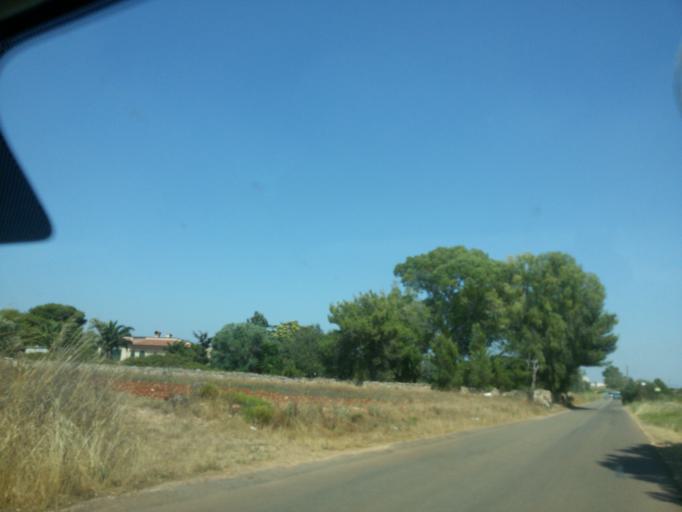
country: IT
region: Apulia
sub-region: Provincia di Lecce
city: Nardo
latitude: 40.1733
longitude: 17.9562
